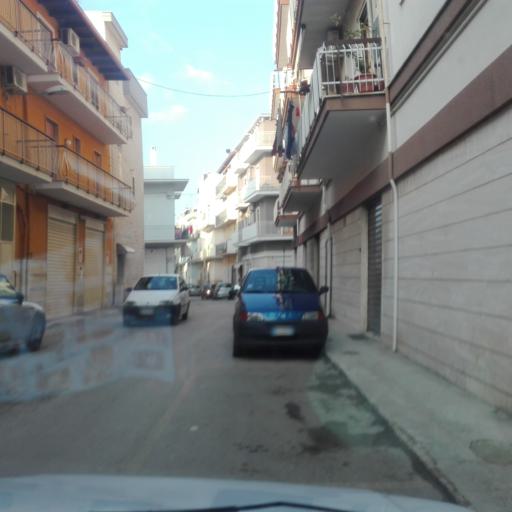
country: IT
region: Apulia
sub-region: Provincia di Bari
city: Corato
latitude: 41.1569
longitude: 16.4074
